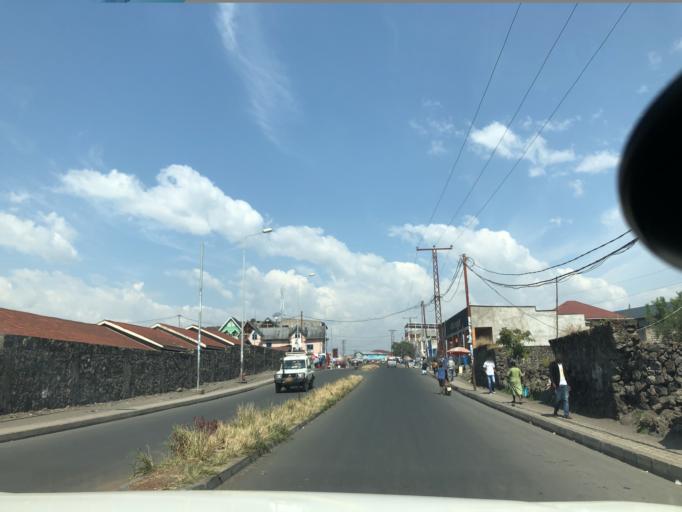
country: CD
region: Nord Kivu
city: Goma
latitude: -1.6571
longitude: 29.1952
